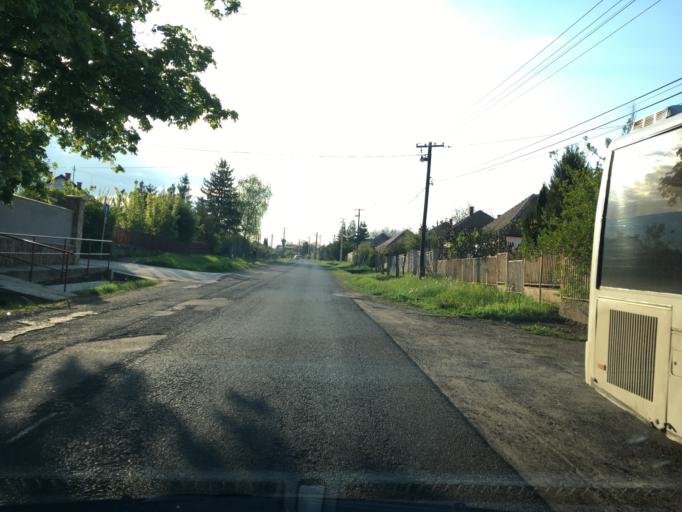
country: HU
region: Nograd
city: Retsag
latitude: 47.8832
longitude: 19.1358
